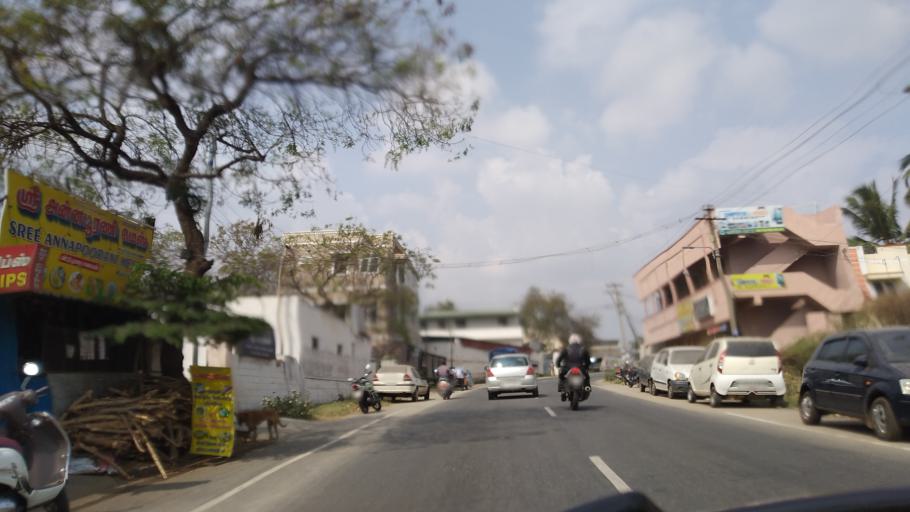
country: IN
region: Tamil Nadu
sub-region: Coimbatore
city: Madukkarai
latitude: 10.9370
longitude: 76.9498
